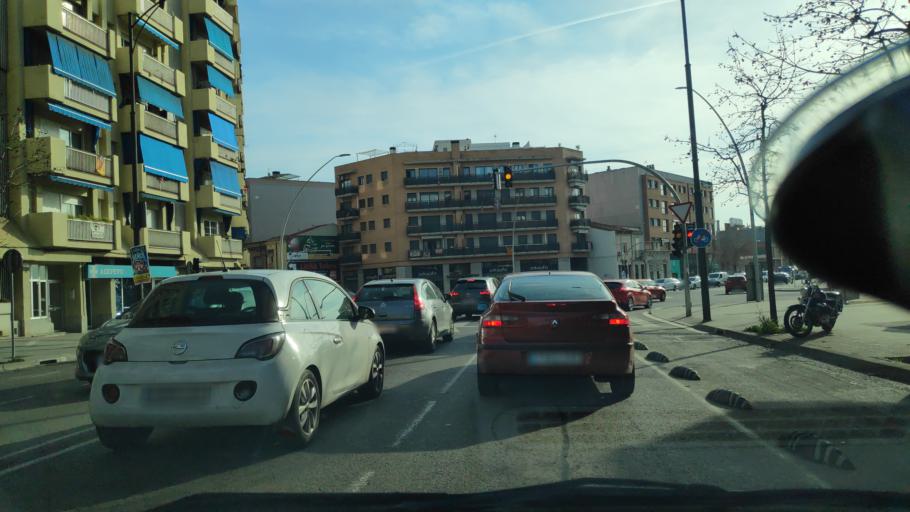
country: ES
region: Catalonia
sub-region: Provincia de Barcelona
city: Sabadell
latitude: 41.5449
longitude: 2.0999
